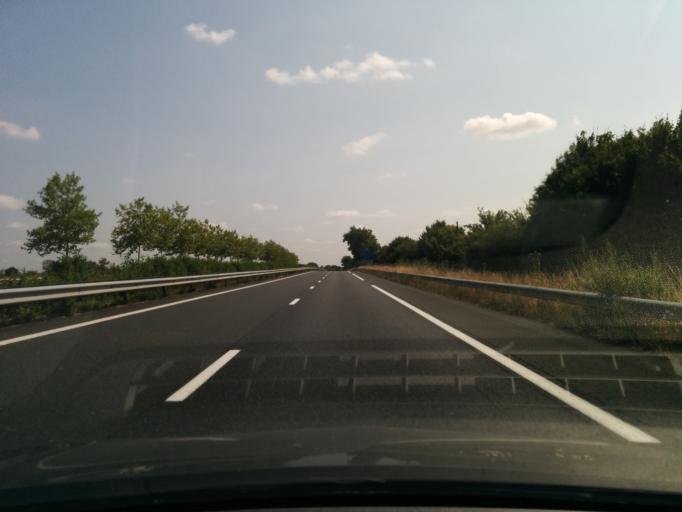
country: FR
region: Centre
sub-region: Departement de l'Indre
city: Montierchaume
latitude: 46.8924
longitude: 1.7294
